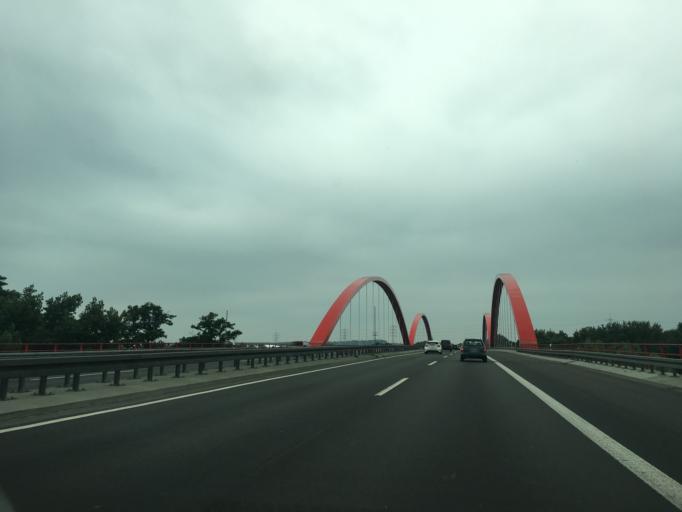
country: DE
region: North Rhine-Westphalia
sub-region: Regierungsbezirk Munster
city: Bottrop
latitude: 51.5042
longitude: 6.9794
